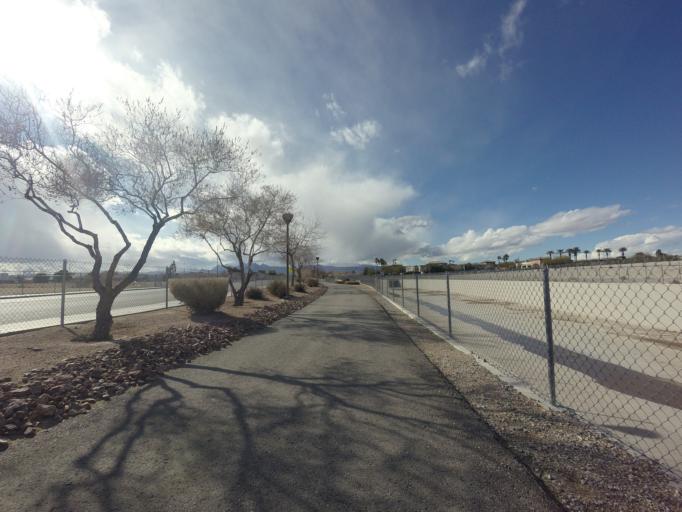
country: US
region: Nevada
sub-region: Clark County
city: North Las Vegas
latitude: 36.2581
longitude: -115.1783
